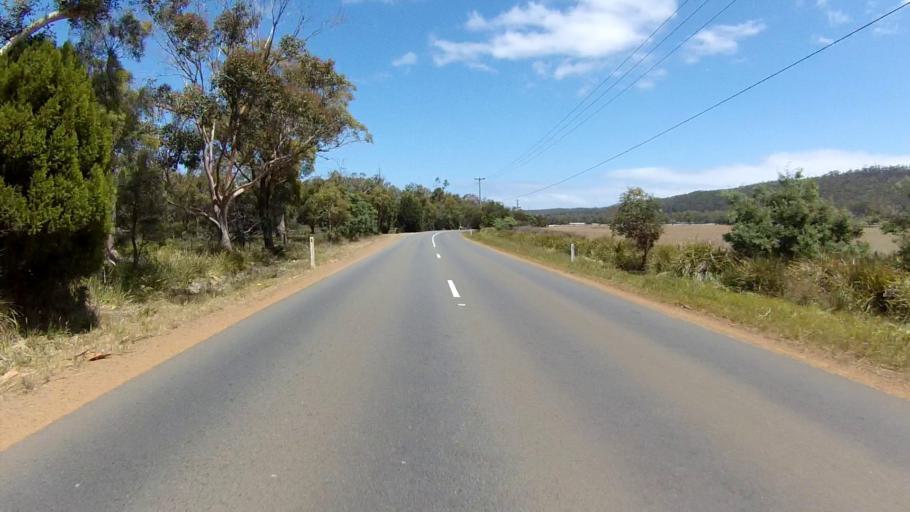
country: AU
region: Tasmania
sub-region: Clarence
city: Sandford
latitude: -42.9403
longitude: 147.4884
